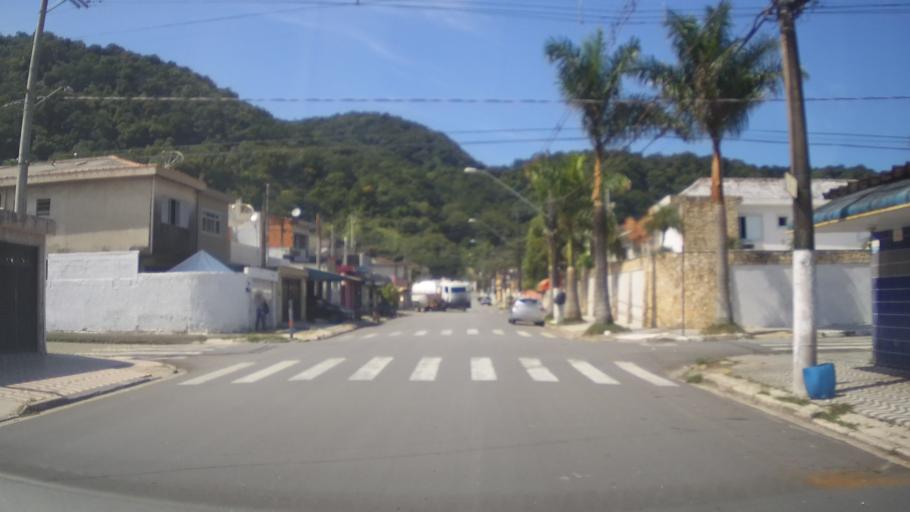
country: BR
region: Sao Paulo
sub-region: Praia Grande
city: Praia Grande
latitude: -23.9857
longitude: -46.3935
